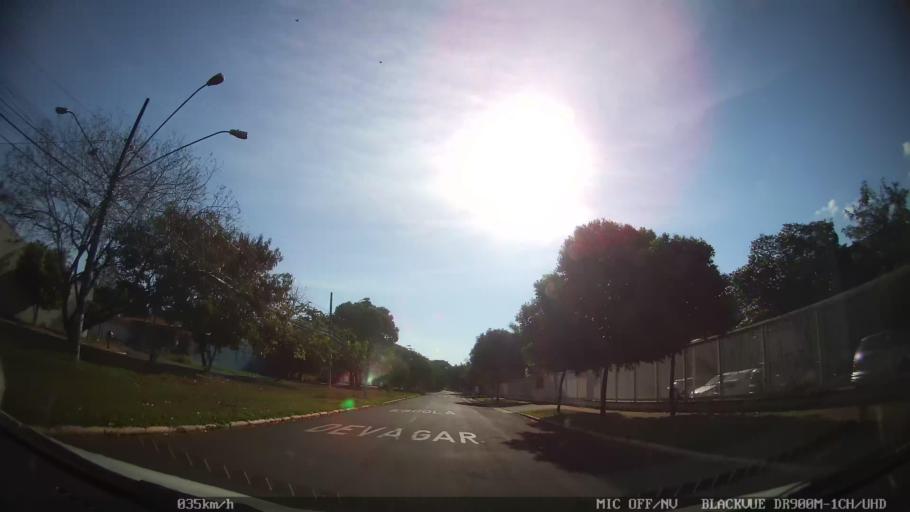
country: BR
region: Sao Paulo
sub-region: Ribeirao Preto
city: Ribeirao Preto
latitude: -21.1925
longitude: -47.7618
